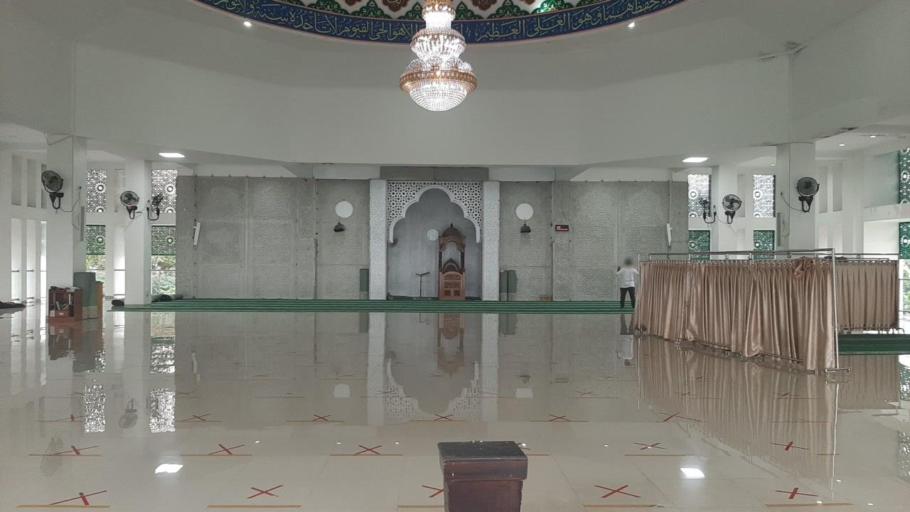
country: ID
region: West Java
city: Cileungsir
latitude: -6.4533
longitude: 107.0427
